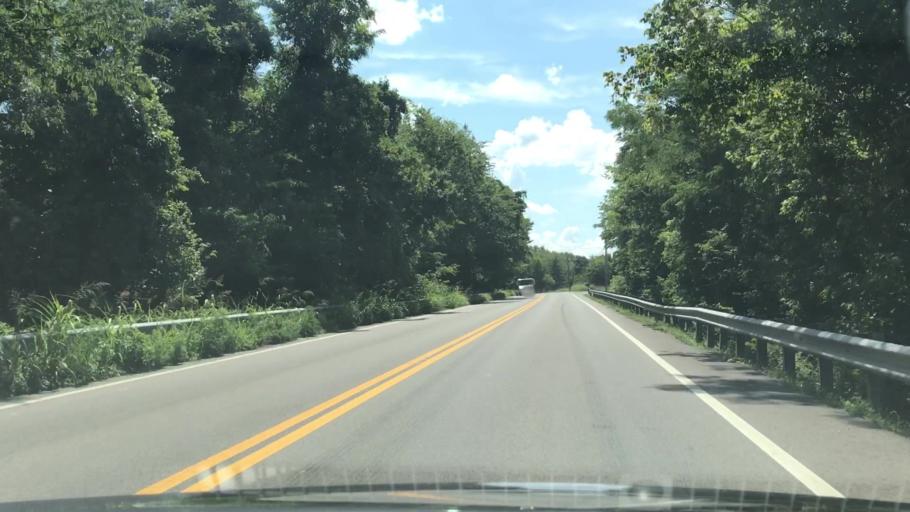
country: US
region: Tennessee
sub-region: Williamson County
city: Franklin
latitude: 35.9019
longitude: -86.7883
